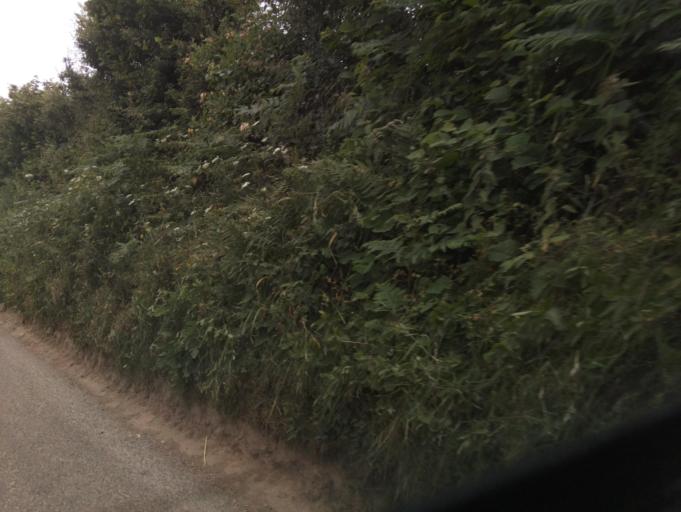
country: GB
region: England
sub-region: Devon
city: Dartmouth
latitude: 50.3638
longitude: -3.6289
